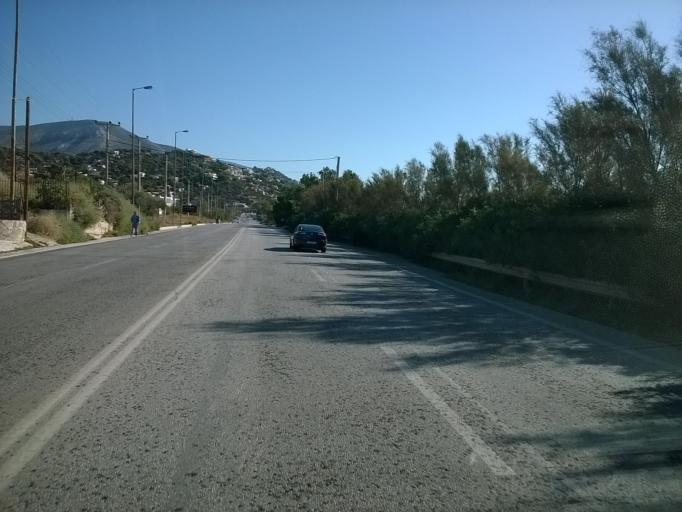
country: GR
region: Attica
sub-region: Nomarchia Anatolikis Attikis
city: Agios Dimitrios Kropias
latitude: 37.8034
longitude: 23.8610
